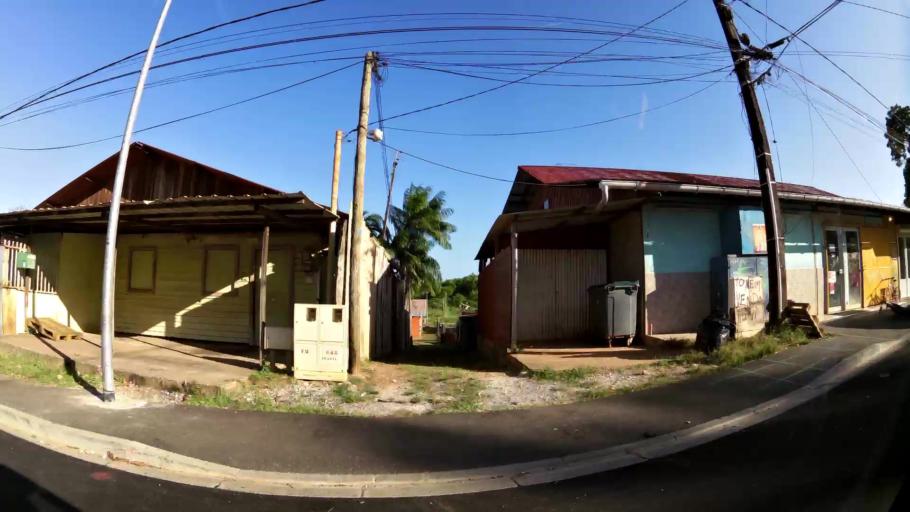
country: GF
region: Guyane
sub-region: Guyane
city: Remire-Montjoly
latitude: 4.8924
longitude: -52.2863
